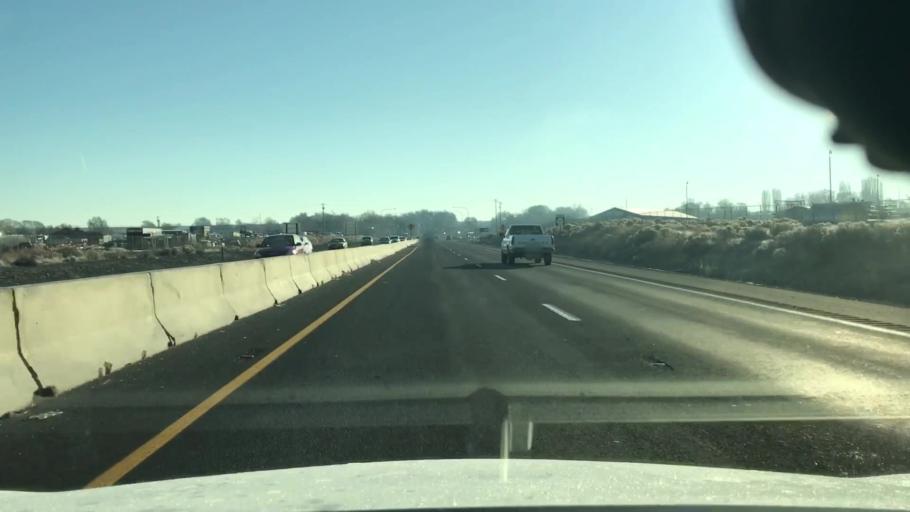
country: US
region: Washington
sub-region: Grant County
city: Moses Lake
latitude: 47.1411
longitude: -119.2675
